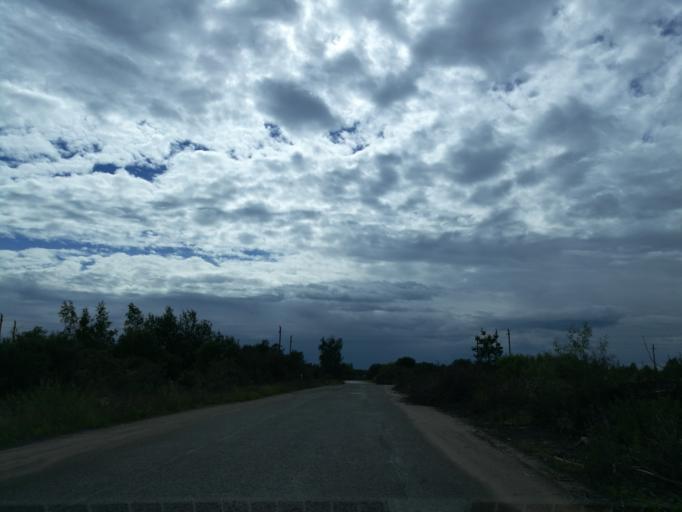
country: LT
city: Trakai
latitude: 54.6176
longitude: 24.9737
